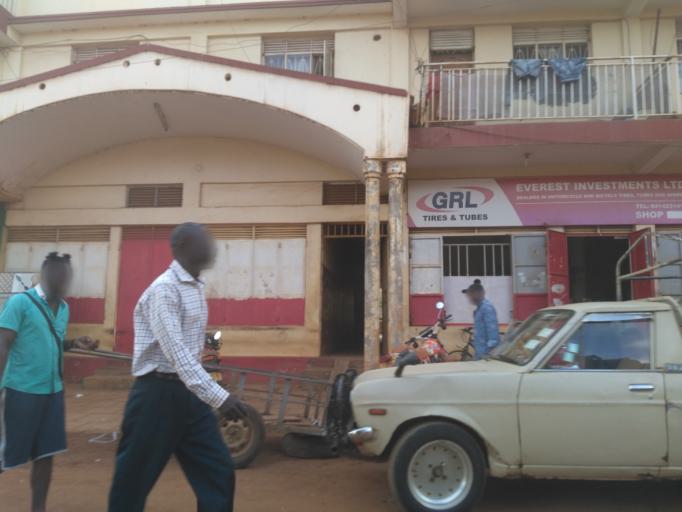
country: UG
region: Eastern Region
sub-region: Jinja District
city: Jinja
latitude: 0.4287
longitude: 33.2126
